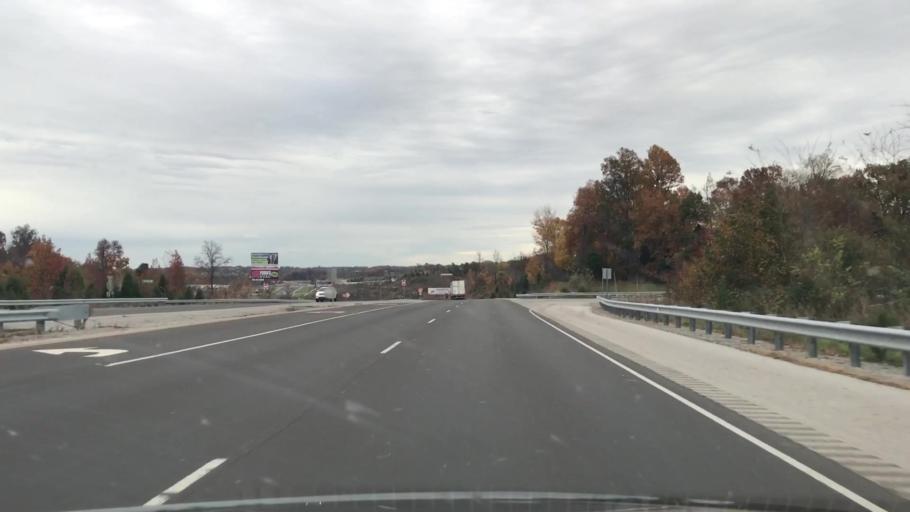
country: US
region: Kentucky
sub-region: Barren County
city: Glasgow
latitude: 37.0151
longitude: -85.9490
